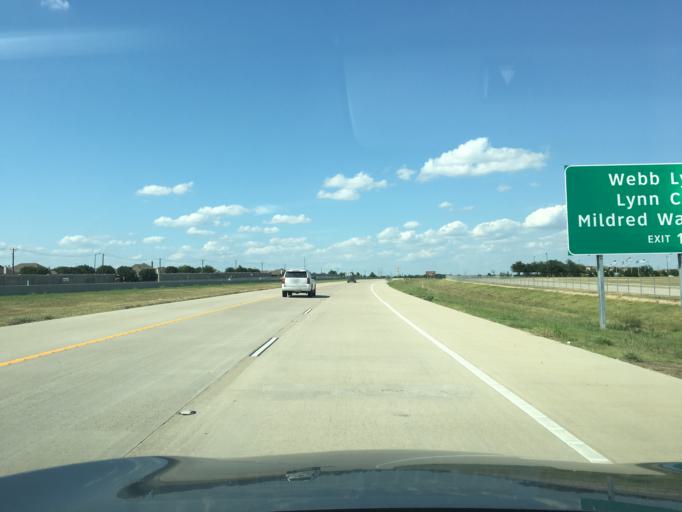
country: US
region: Texas
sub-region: Tarrant County
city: Mansfield
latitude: 32.6148
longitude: -97.0763
